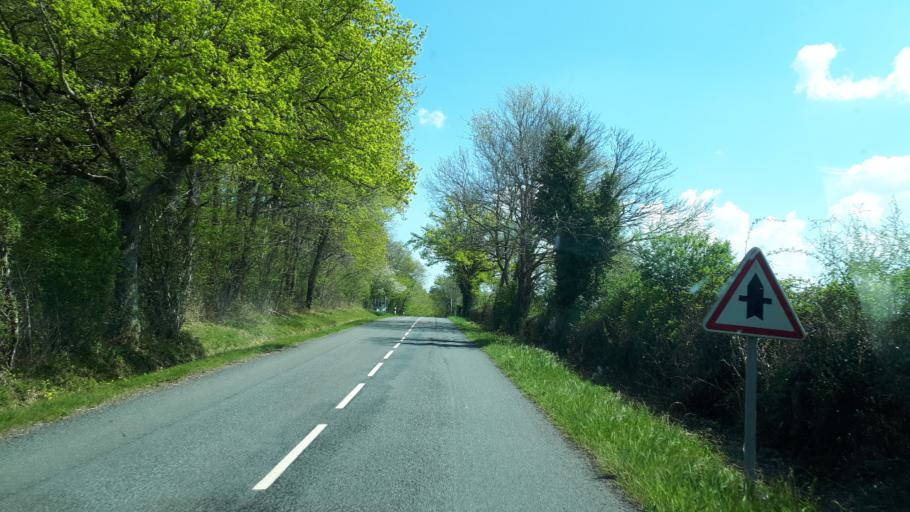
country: FR
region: Centre
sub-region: Departement du Cher
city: Rians
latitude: 47.2998
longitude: 2.6745
